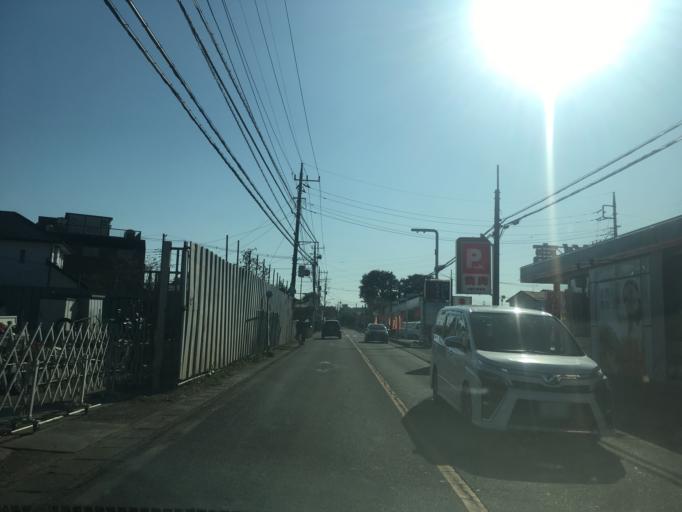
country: JP
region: Saitama
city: Kamifukuoka
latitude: 35.8593
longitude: 139.4700
